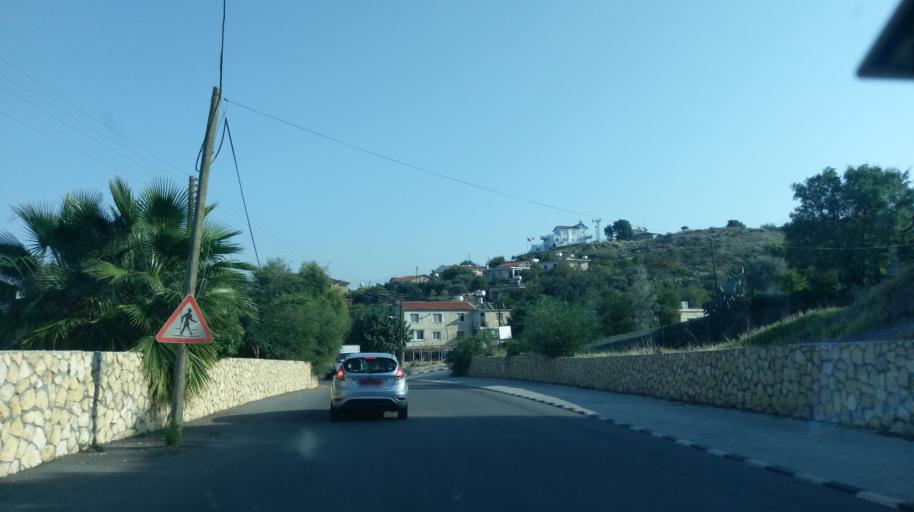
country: CY
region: Lefkosia
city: Lefka
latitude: 35.1494
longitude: 32.7995
